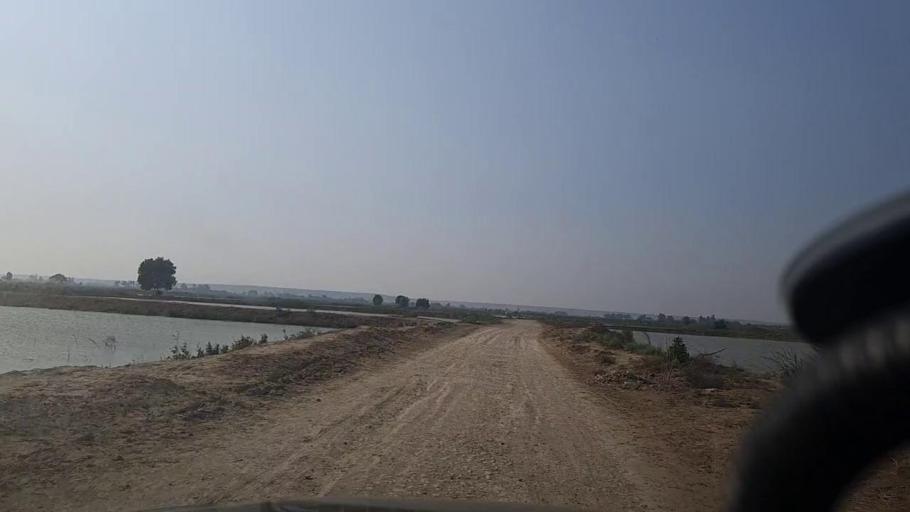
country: PK
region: Sindh
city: Thatta
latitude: 24.6156
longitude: 67.8869
